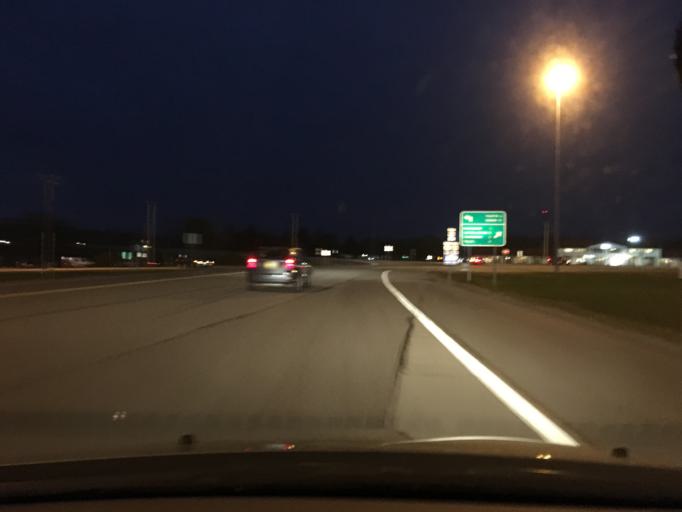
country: US
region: New York
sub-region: Ontario County
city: Manchester
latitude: 42.9762
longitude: -77.2290
